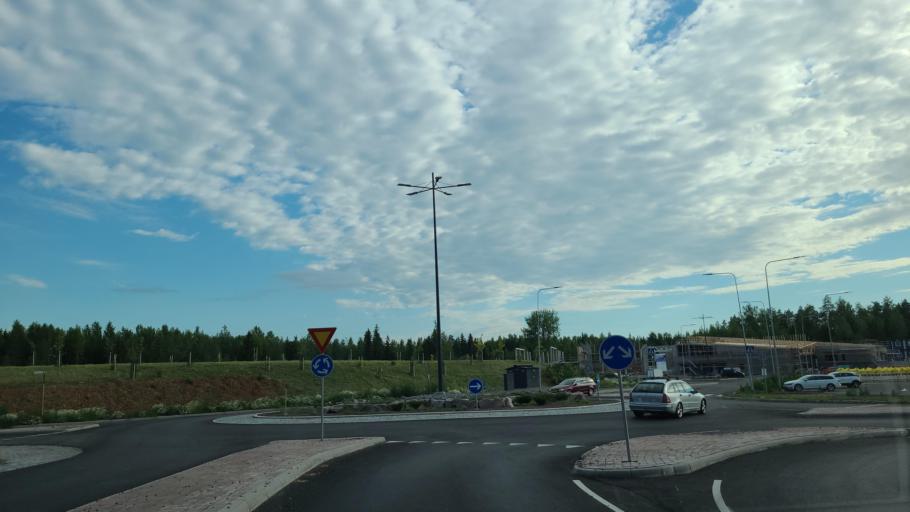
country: FI
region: Varsinais-Suomi
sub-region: Turku
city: Naantali
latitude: 60.4563
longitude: 21.9903
